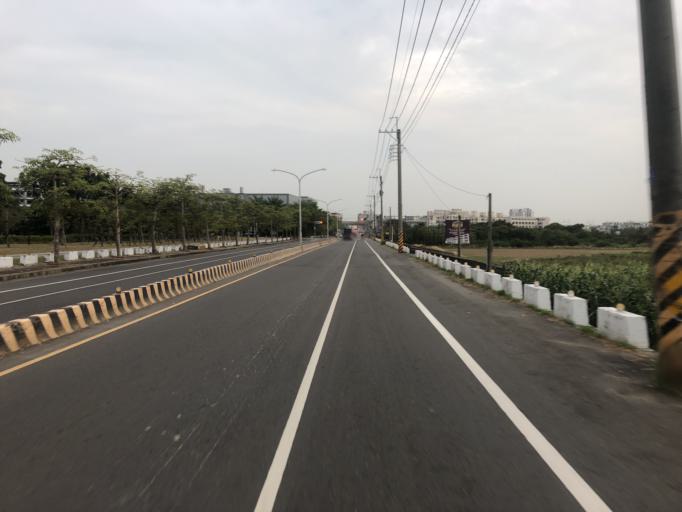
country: TW
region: Taiwan
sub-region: Tainan
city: Tainan
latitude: 23.0837
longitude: 120.2816
